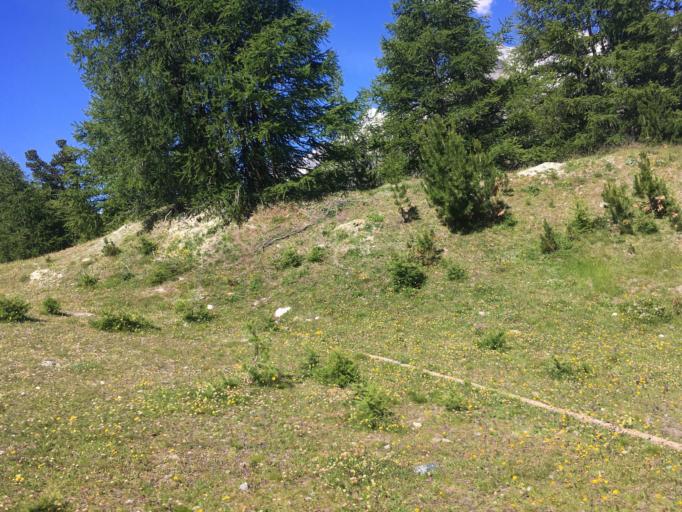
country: CH
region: Valais
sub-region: Visp District
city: Zermatt
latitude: 46.0043
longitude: 7.7573
